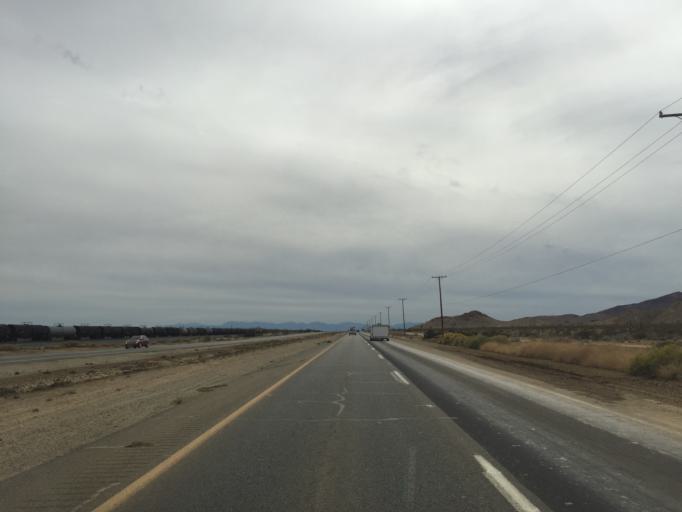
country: US
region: California
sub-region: Kern County
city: Mojave
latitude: 35.0217
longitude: -118.1650
